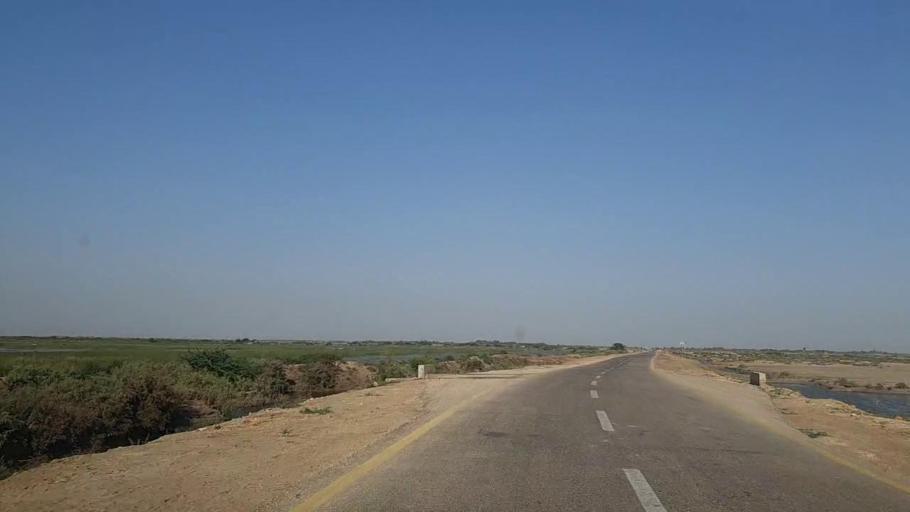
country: PK
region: Sindh
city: Jati
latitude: 24.4408
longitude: 68.3199
